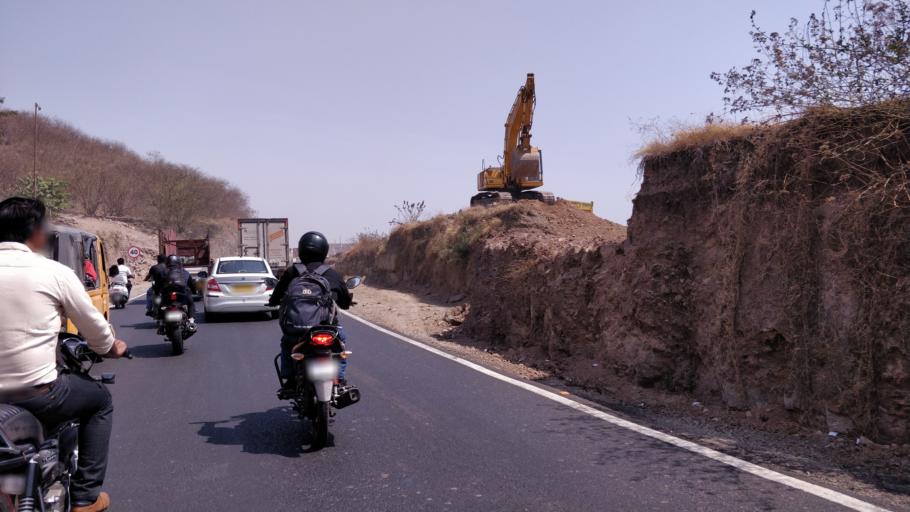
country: IN
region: Maharashtra
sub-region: Pune Division
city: Shivaji Nagar
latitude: 18.5346
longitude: 73.7802
